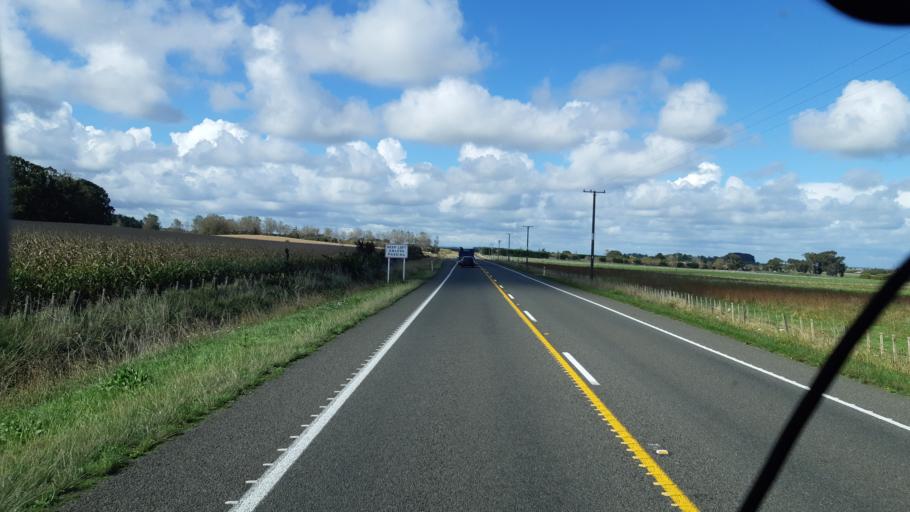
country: NZ
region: Manawatu-Wanganui
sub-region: Wanganui District
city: Wanganui
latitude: -39.9792
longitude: 175.1392
